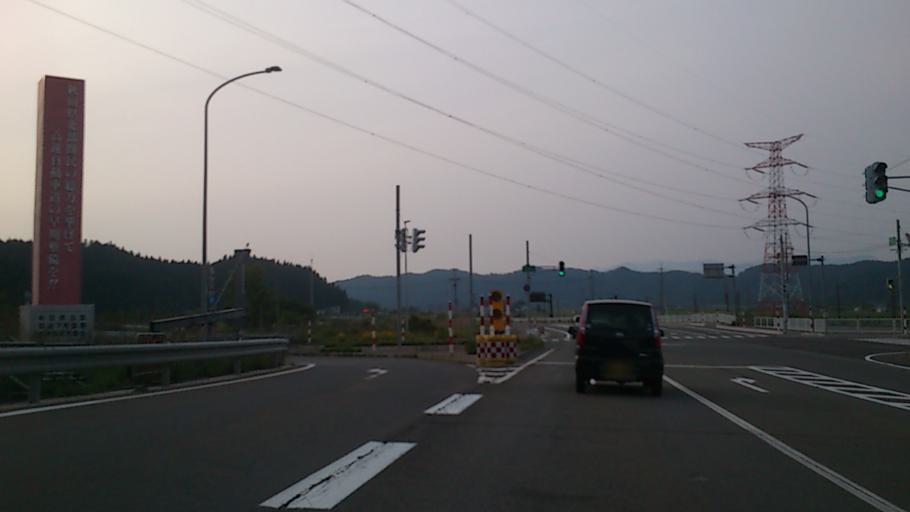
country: JP
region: Akita
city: Noshiromachi
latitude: 40.2111
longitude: 140.1992
